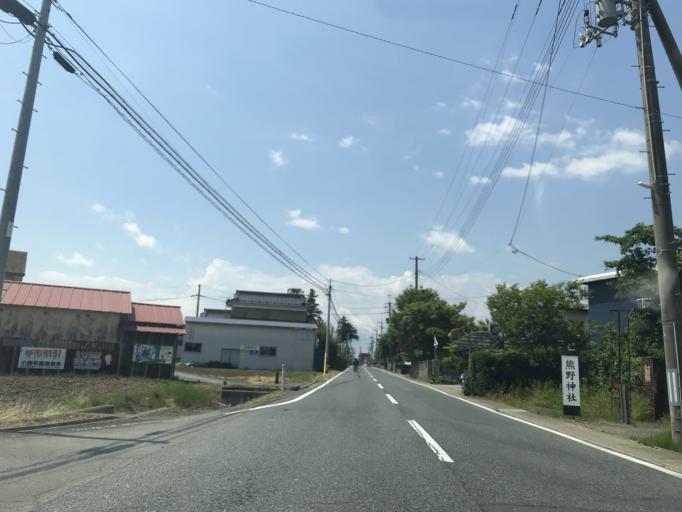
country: JP
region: Miyagi
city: Kogota
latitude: 38.5834
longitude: 141.0351
